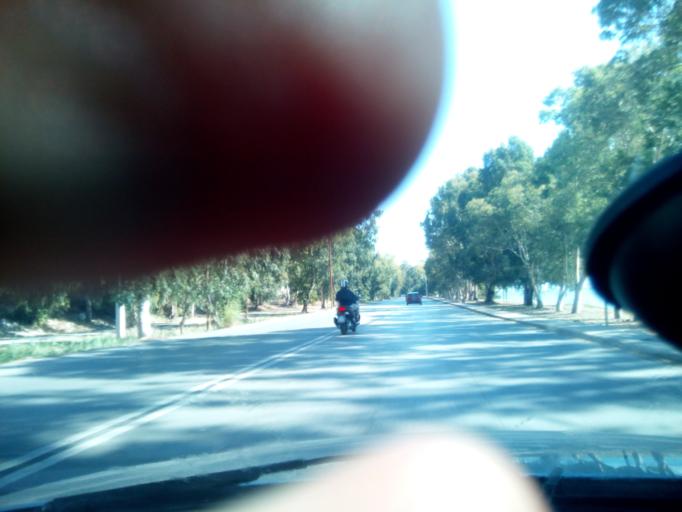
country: GR
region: Central Greece
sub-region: Nomos Evvoias
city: Chalkida
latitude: 38.4527
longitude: 23.6138
